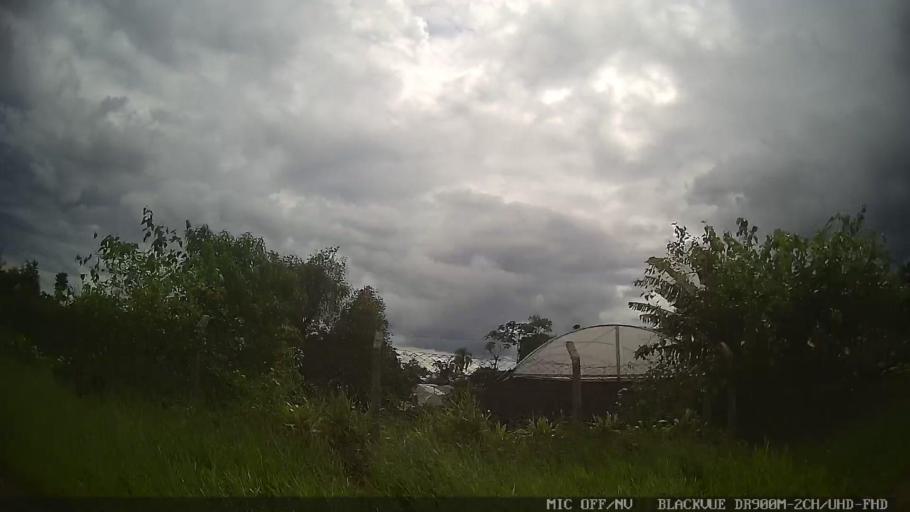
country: BR
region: Sao Paulo
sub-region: Suzano
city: Suzano
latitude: -23.6292
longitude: -46.2819
